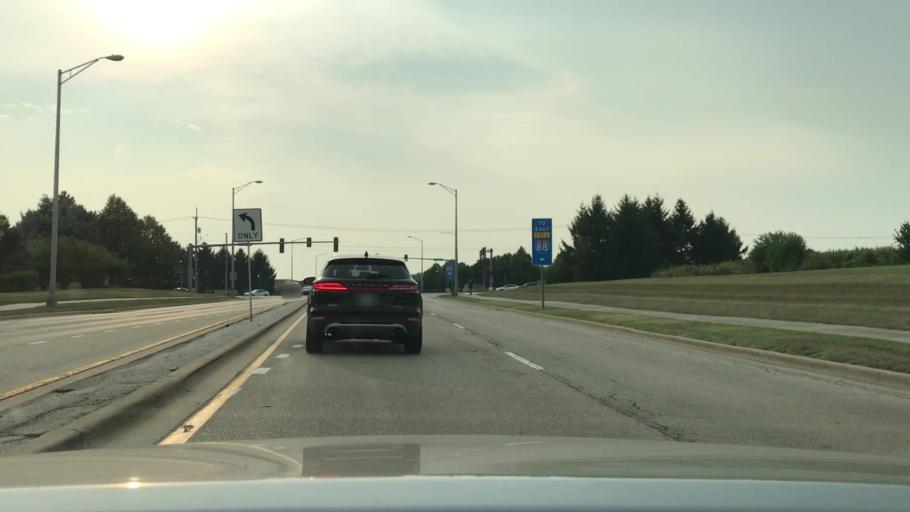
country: US
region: Illinois
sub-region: DuPage County
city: Warrenville
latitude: 41.8077
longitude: -88.2363
